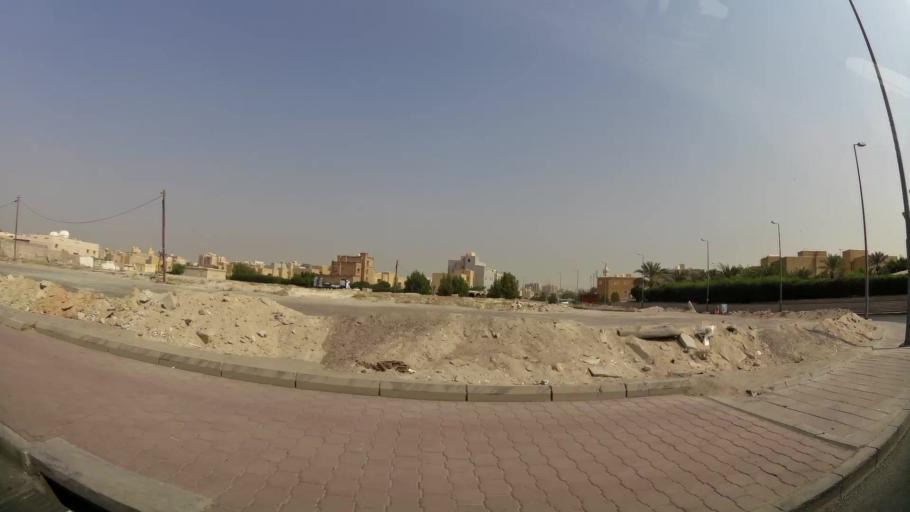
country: KW
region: Al Farwaniyah
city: Al Farwaniyah
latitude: 29.2486
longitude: 47.9320
